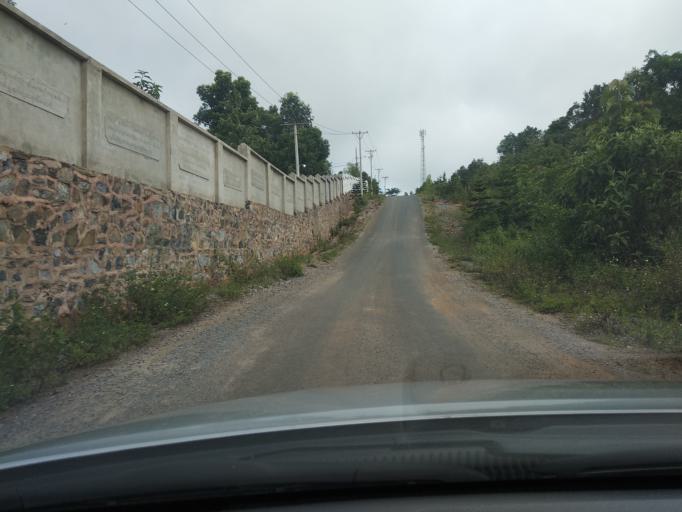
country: MM
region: Mandalay
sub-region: Pyin Oo Lwin District
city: Pyin Oo Lwin
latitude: 21.9224
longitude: 96.3760
